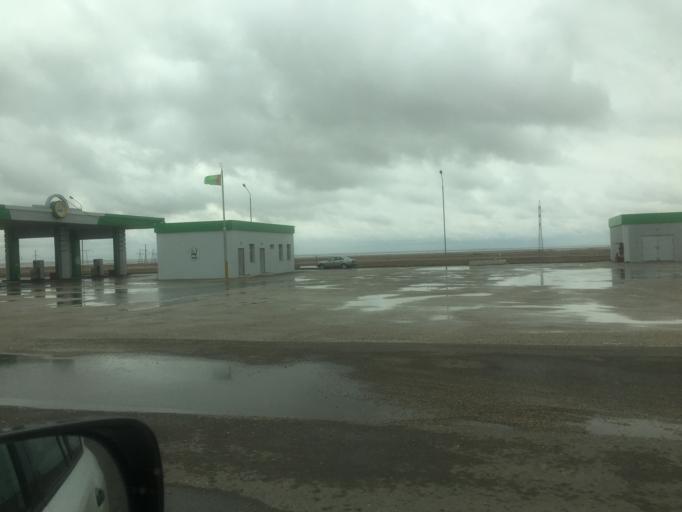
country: TM
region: Balkan
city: Balkanabat
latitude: 39.9302
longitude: 53.8646
